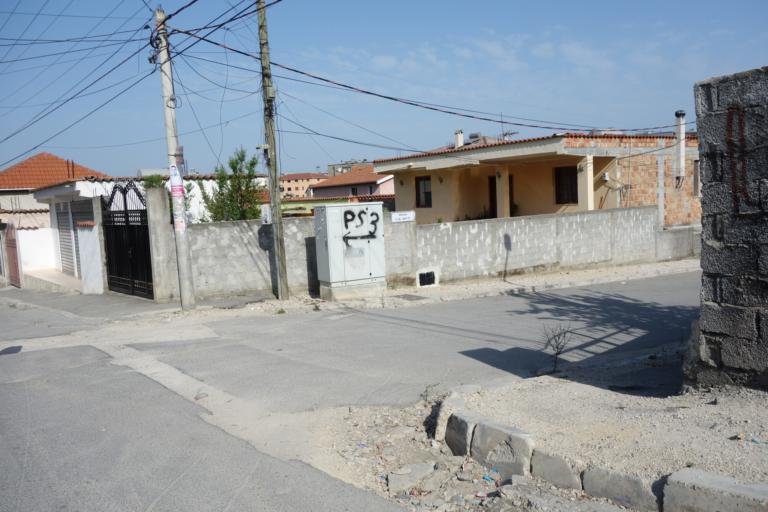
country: AL
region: Tirane
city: Tirana
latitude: 41.3373
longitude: 19.8470
